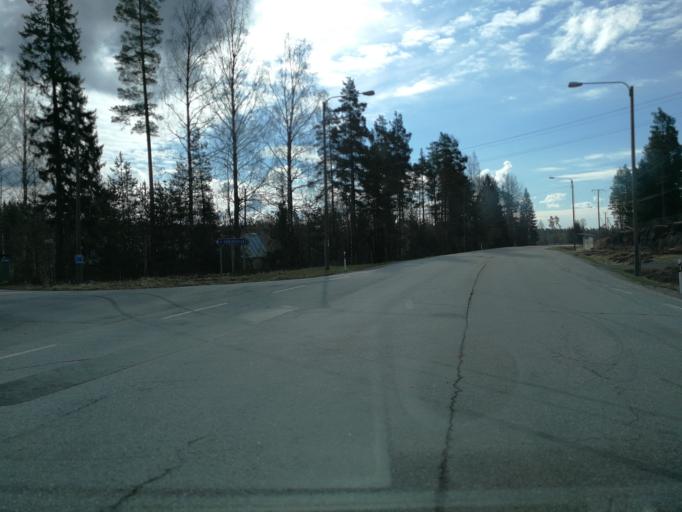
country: FI
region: Uusimaa
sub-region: Helsinki
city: Karjalohja
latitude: 60.2100
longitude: 23.6681
